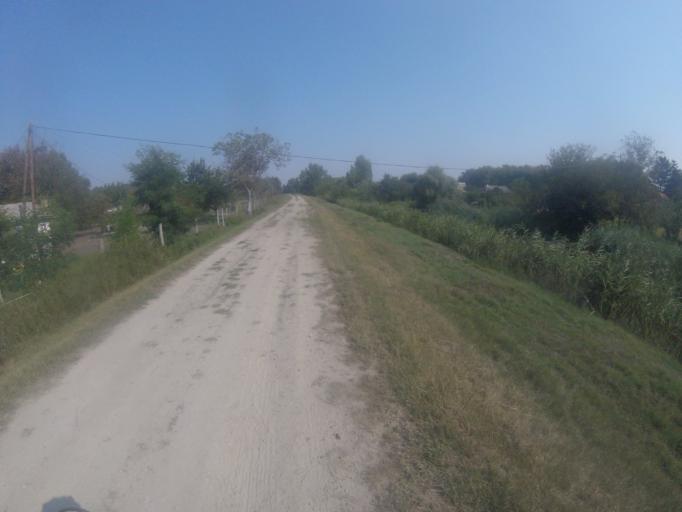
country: HU
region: Bacs-Kiskun
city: Baja
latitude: 46.2081
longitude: 18.9569
